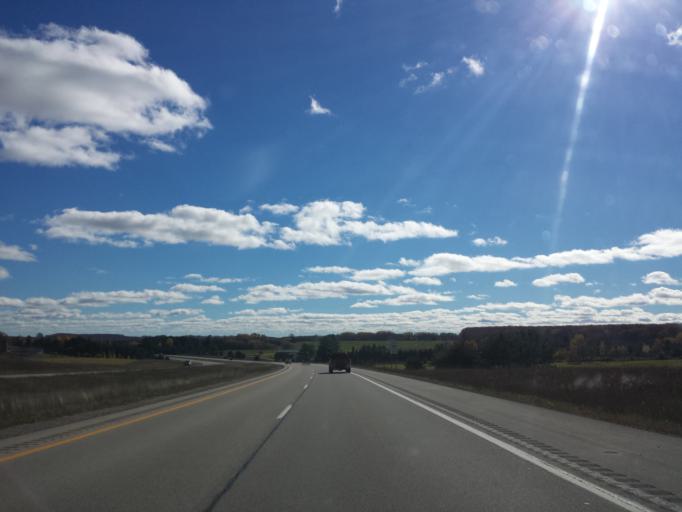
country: US
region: Michigan
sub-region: Cheboygan County
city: Cheboygan
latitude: 45.6257
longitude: -84.6346
